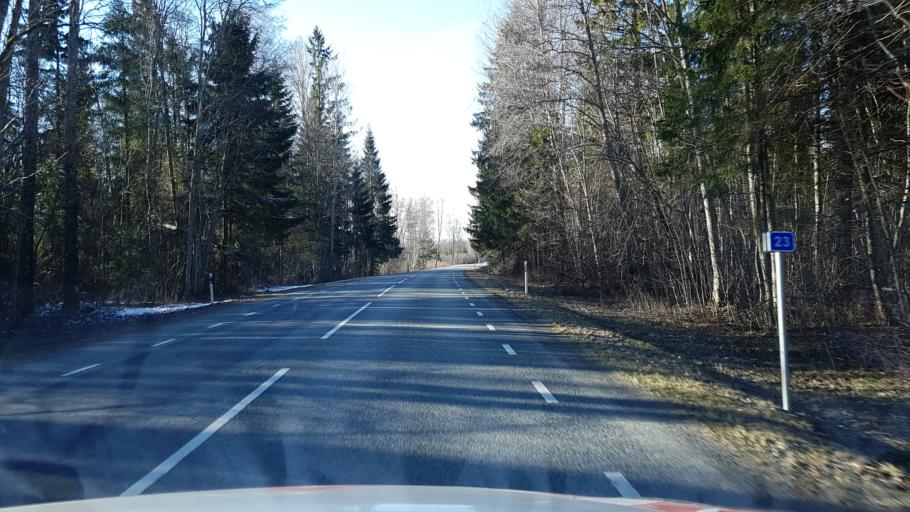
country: EE
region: Laeaene-Virumaa
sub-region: Tapa vald
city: Tapa
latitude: 59.4363
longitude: 25.9627
